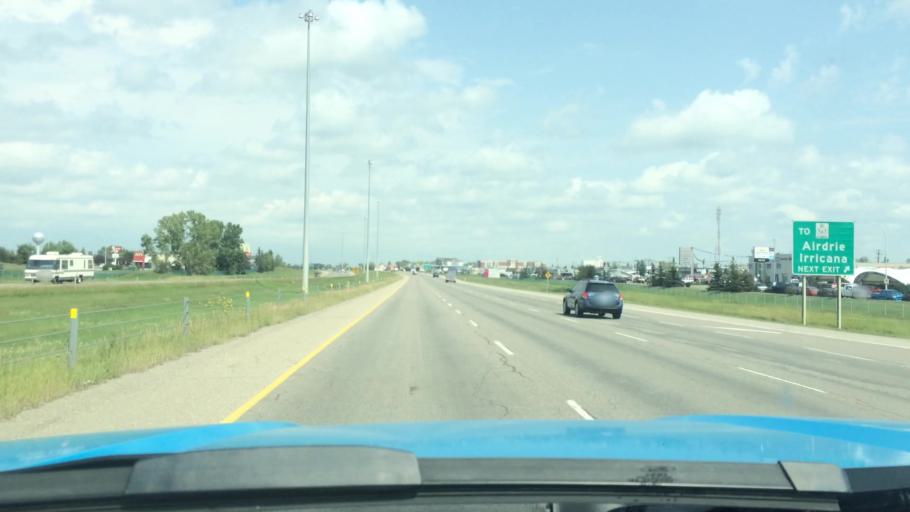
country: CA
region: Alberta
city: Airdrie
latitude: 51.2869
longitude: -114.0005
